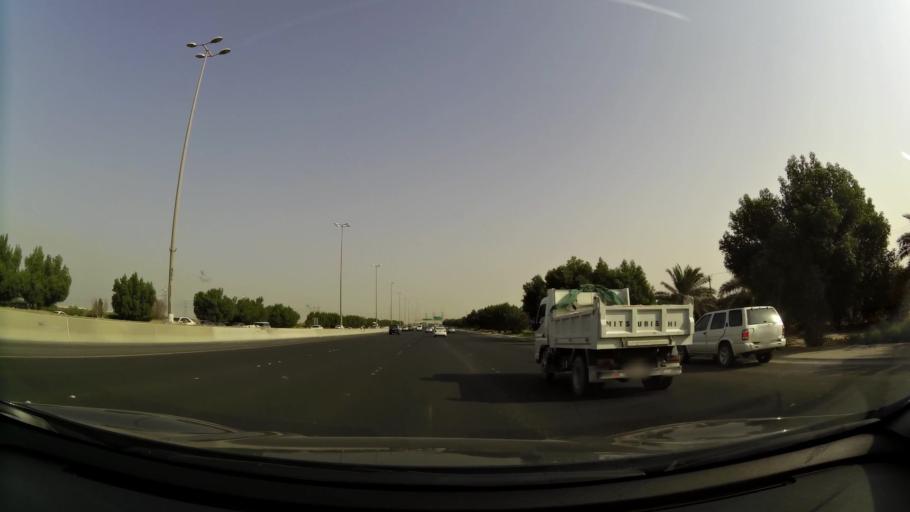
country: KW
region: Muhafazat al Jahra'
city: Al Jahra'
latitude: 29.3156
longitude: 47.7681
